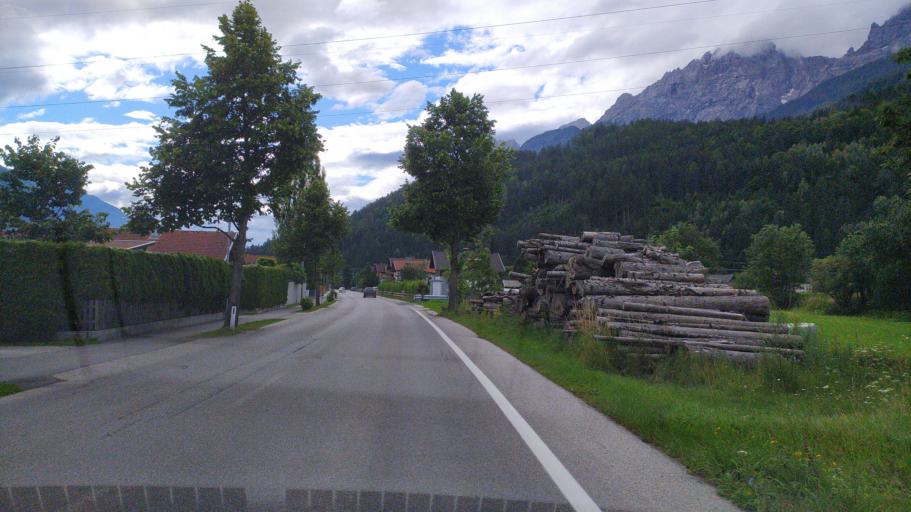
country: AT
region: Tyrol
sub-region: Politischer Bezirk Lienz
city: Tristach
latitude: 46.8173
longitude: 12.7956
